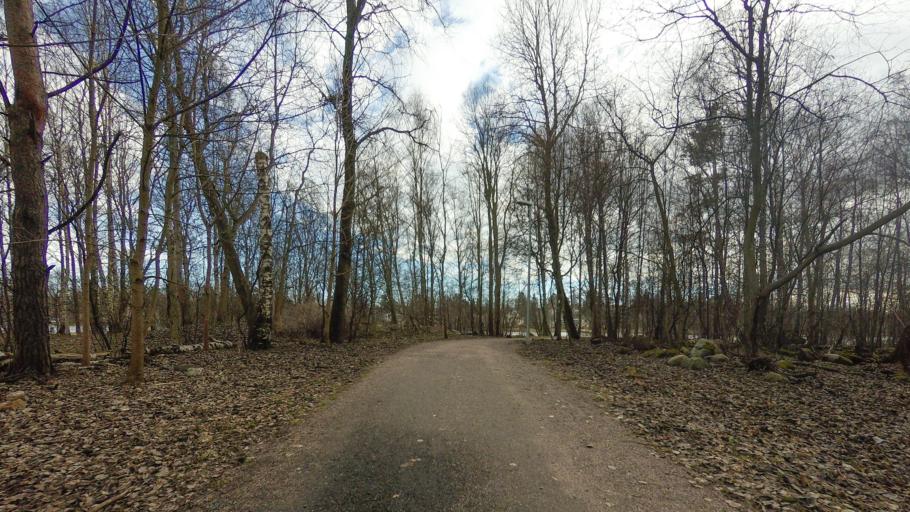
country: FI
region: Uusimaa
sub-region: Helsinki
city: Vantaa
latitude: 60.1939
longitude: 25.0533
